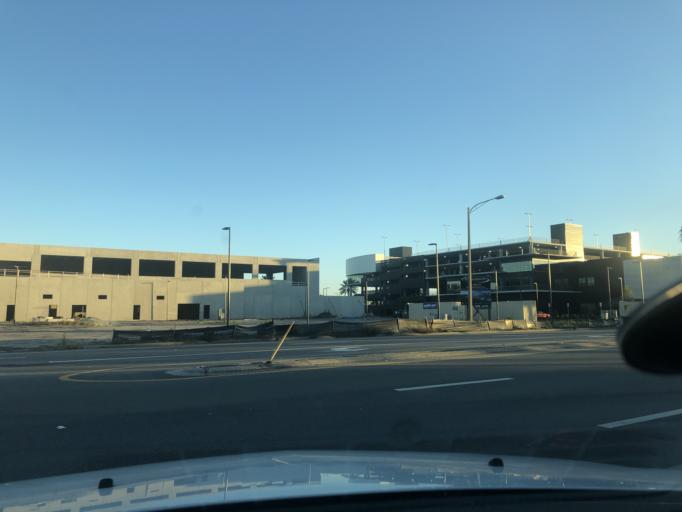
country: US
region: Florida
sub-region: Orange County
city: Oak Ridge
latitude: 28.4902
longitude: -81.4393
